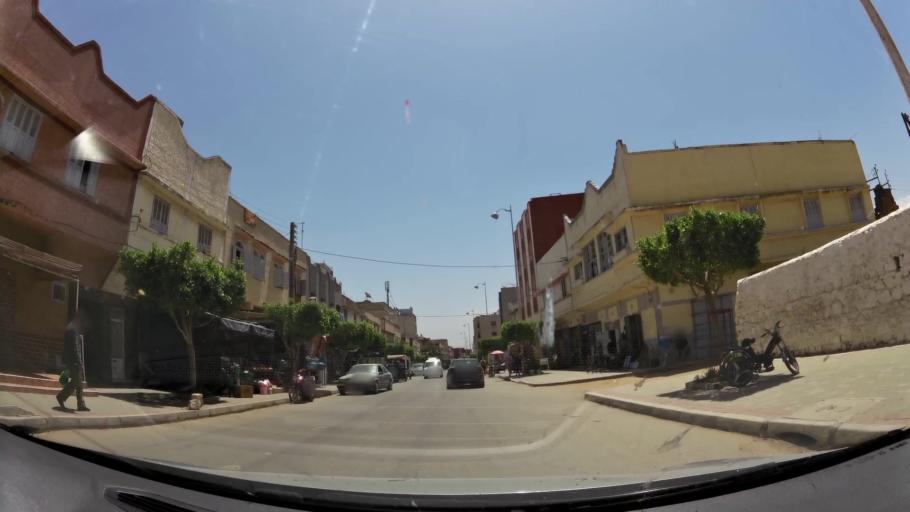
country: MA
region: Rabat-Sale-Zemmour-Zaer
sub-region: Khemisset
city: Khemisset
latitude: 33.8308
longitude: -6.0737
